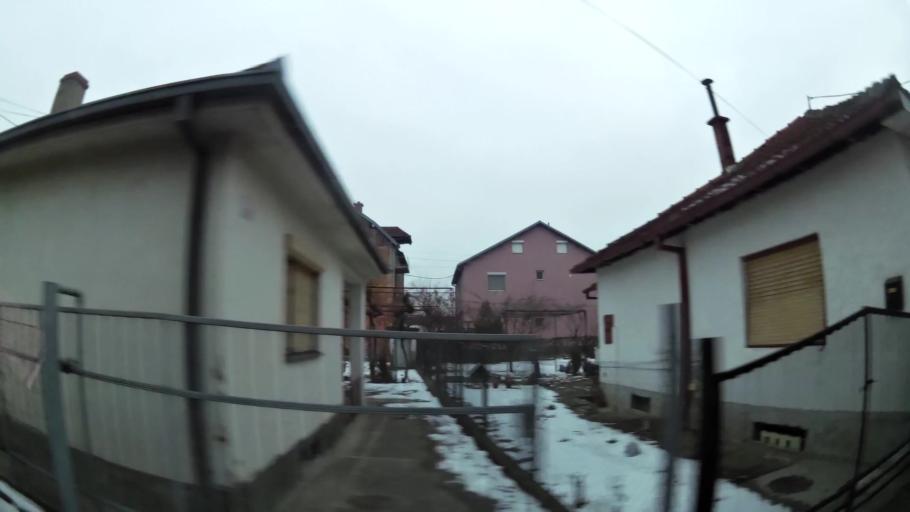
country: MK
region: Kisela Voda
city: Usje
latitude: 41.9747
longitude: 21.4831
